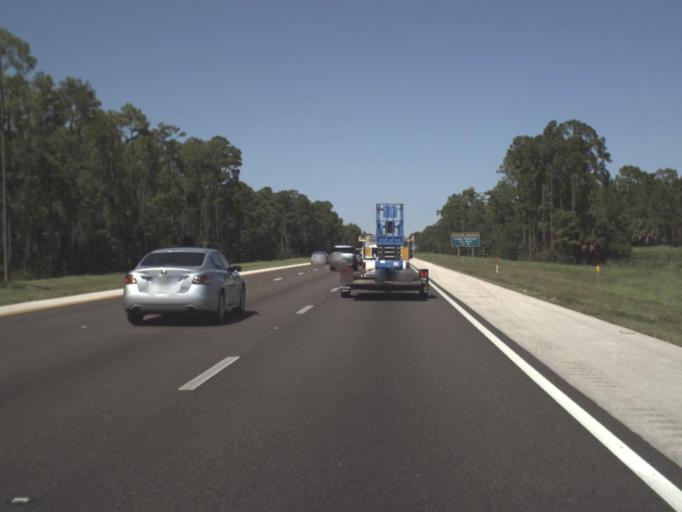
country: US
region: Florida
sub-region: Collier County
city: Vineyards
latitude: 26.2523
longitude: -81.7389
